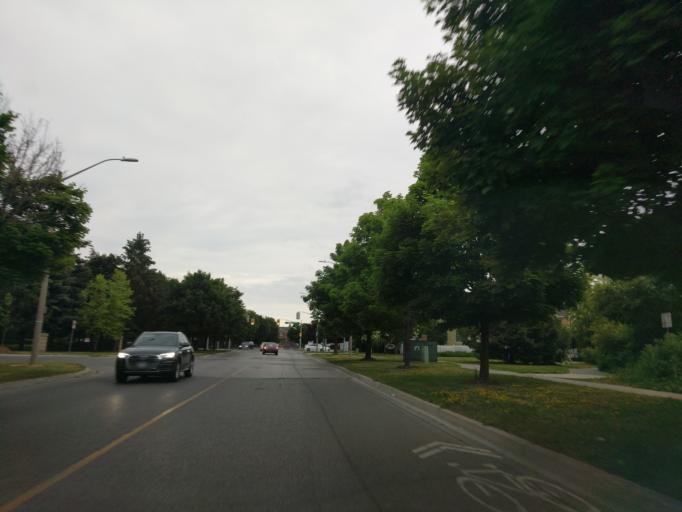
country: CA
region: Ontario
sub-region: York
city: Richmond Hill
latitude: 43.8625
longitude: -79.4316
